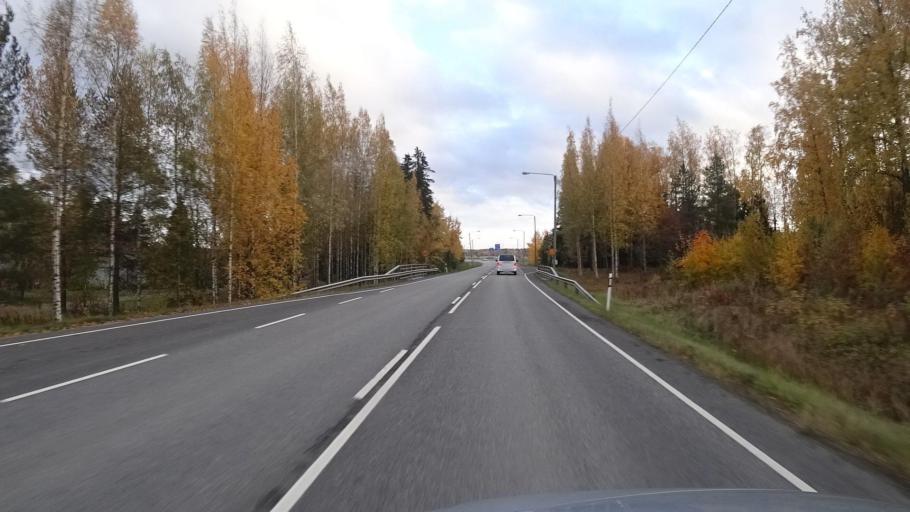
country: FI
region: Varsinais-Suomi
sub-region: Loimaa
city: Loimaa
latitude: 60.8722
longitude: 23.0002
